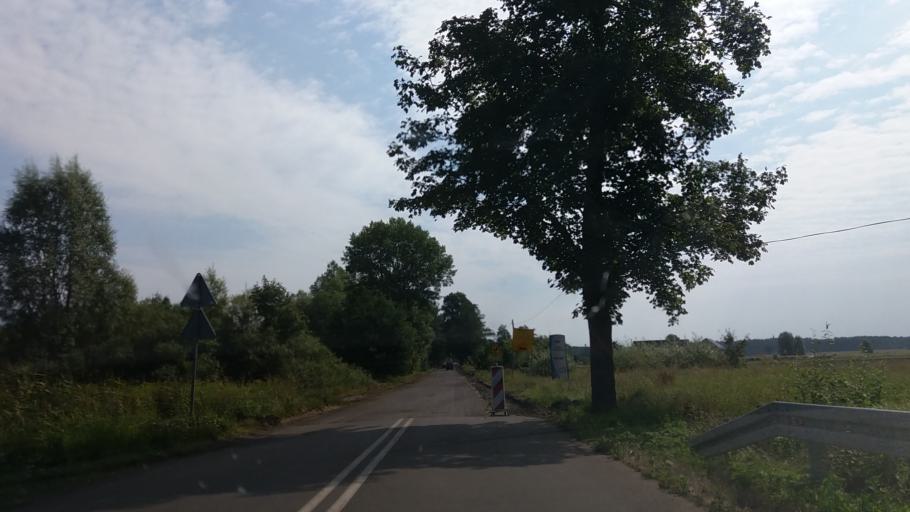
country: PL
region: Lubusz
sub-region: Powiat strzelecko-drezdenecki
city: Stare Kurowo
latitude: 52.7738
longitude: 15.6404
